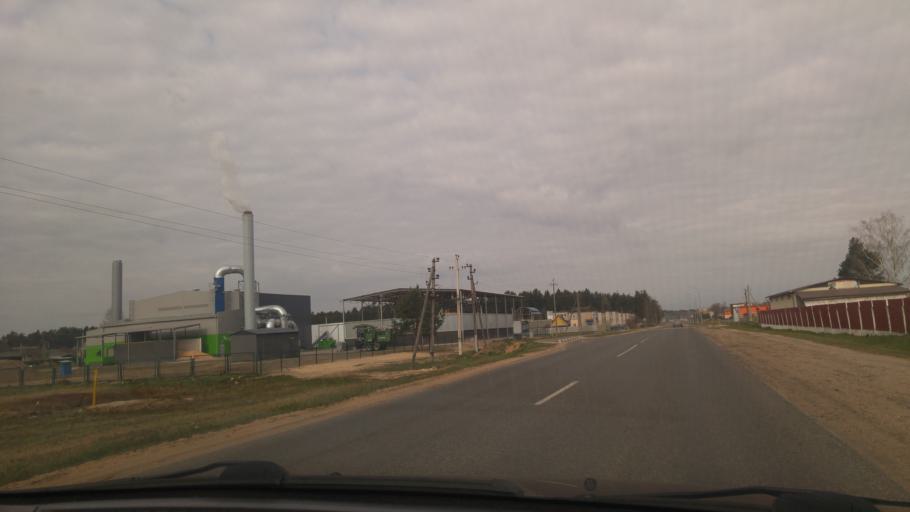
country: BY
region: Minsk
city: Chervyen'
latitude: 53.6972
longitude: 28.4261
